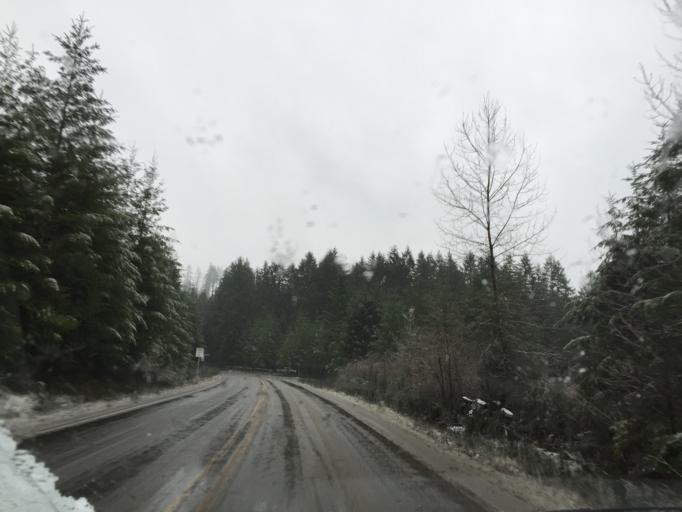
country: US
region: Washington
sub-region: Thurston County
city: Rochester
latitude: 46.9470
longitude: -123.0708
